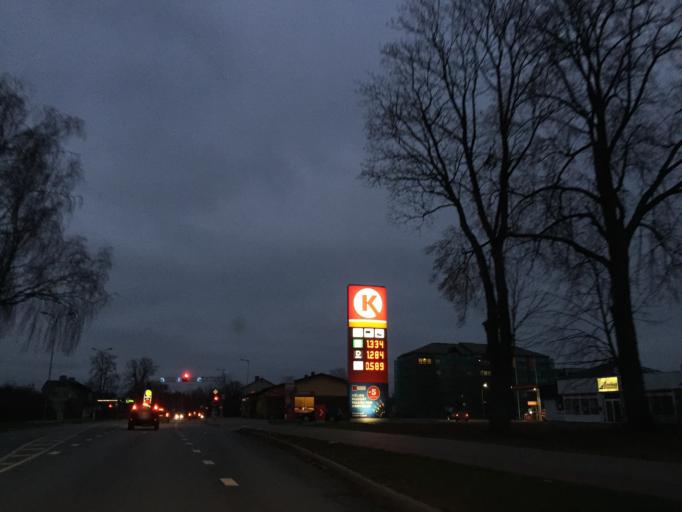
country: LV
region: Valmieras Rajons
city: Valmiera
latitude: 57.5305
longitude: 25.3906
